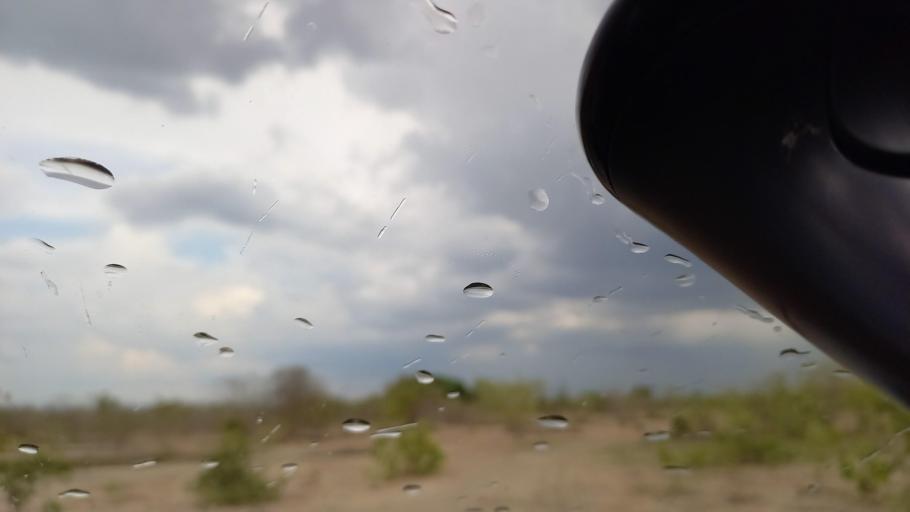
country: ZM
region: Lusaka
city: Kafue
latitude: -15.8550
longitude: 28.1156
